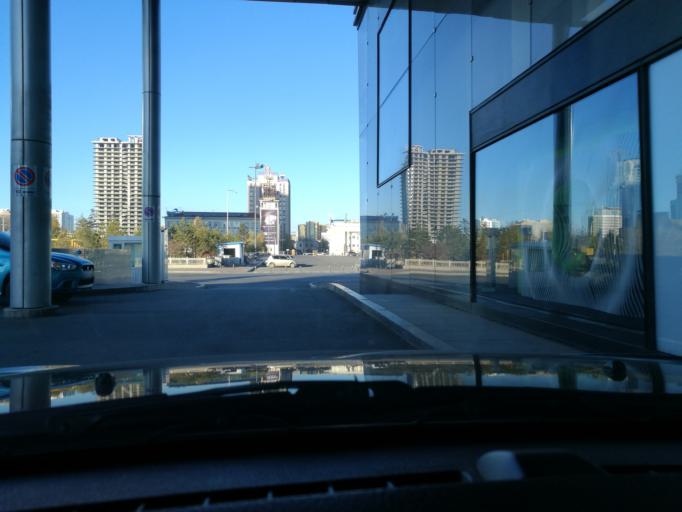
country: MN
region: Ulaanbaatar
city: Ulaanbaatar
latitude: 47.9181
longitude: 106.9198
